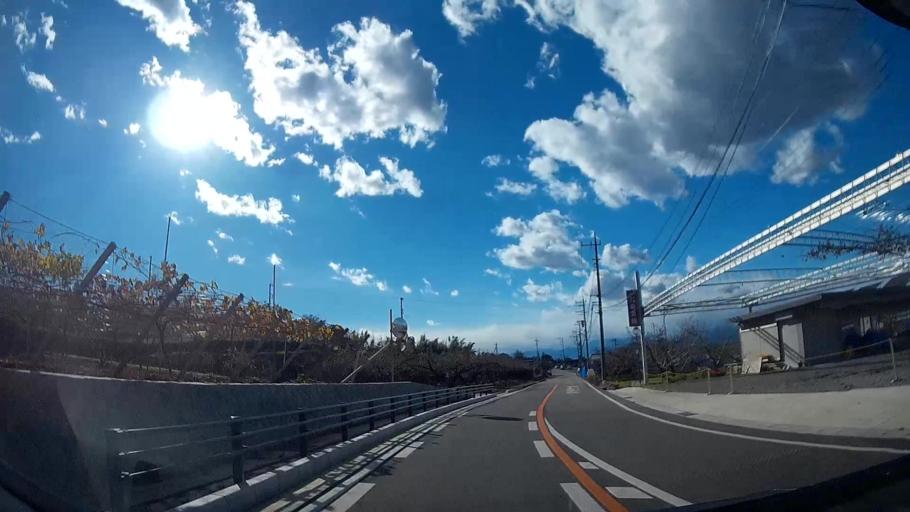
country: JP
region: Yamanashi
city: Enzan
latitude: 35.6376
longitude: 138.7073
